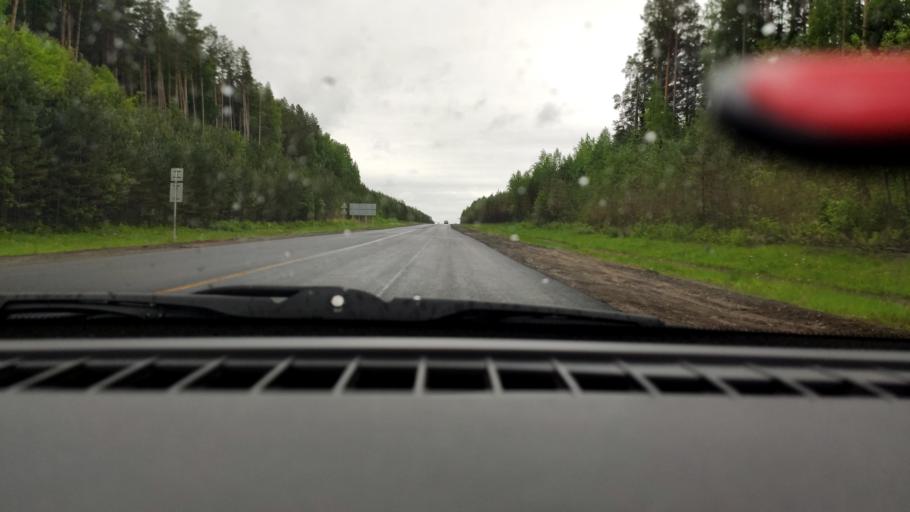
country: RU
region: Perm
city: Karagay
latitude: 58.2574
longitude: 54.8892
